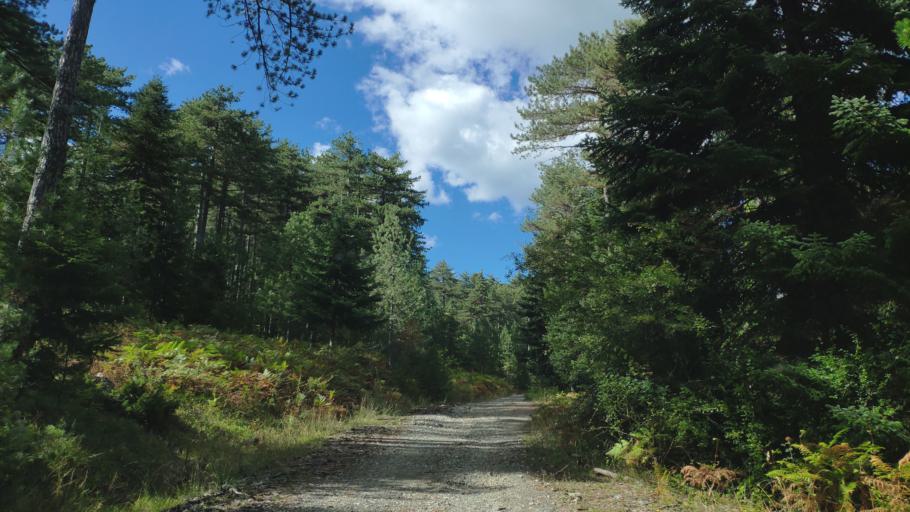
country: GR
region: Epirus
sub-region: Nomos Ioanninon
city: Metsovo
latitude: 39.8891
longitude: 21.2512
